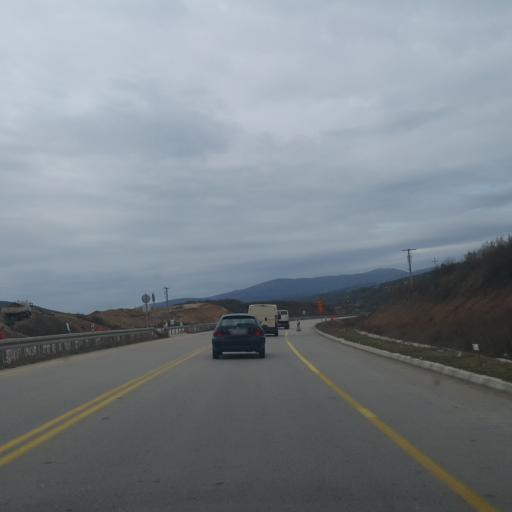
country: RS
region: Central Serbia
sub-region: Pirotski Okrug
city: Pirot
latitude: 43.2147
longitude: 22.5058
